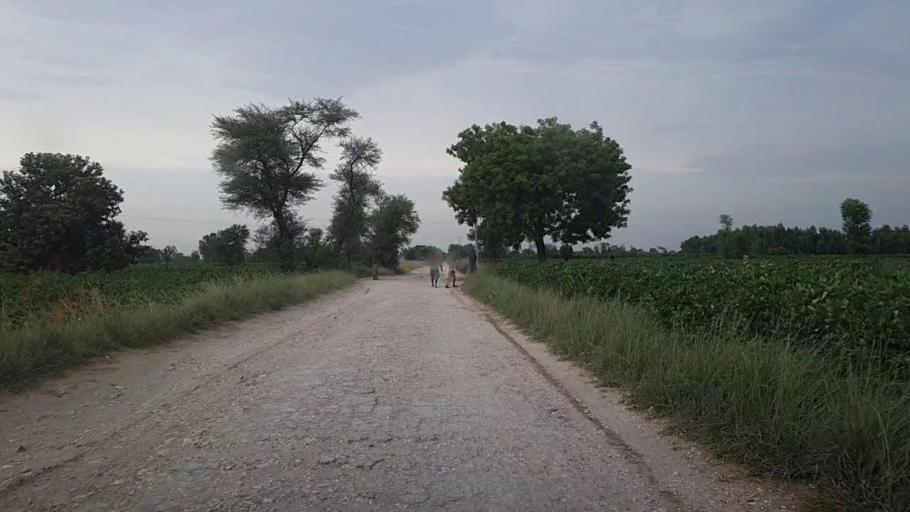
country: PK
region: Sindh
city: Karaundi
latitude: 26.9756
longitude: 68.3438
